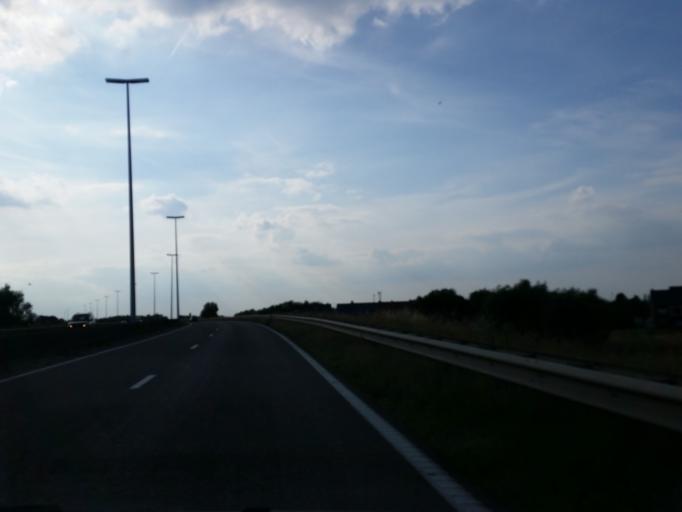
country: BE
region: Flanders
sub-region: Provincie Antwerpen
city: Willebroek
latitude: 51.0466
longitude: 4.3440
